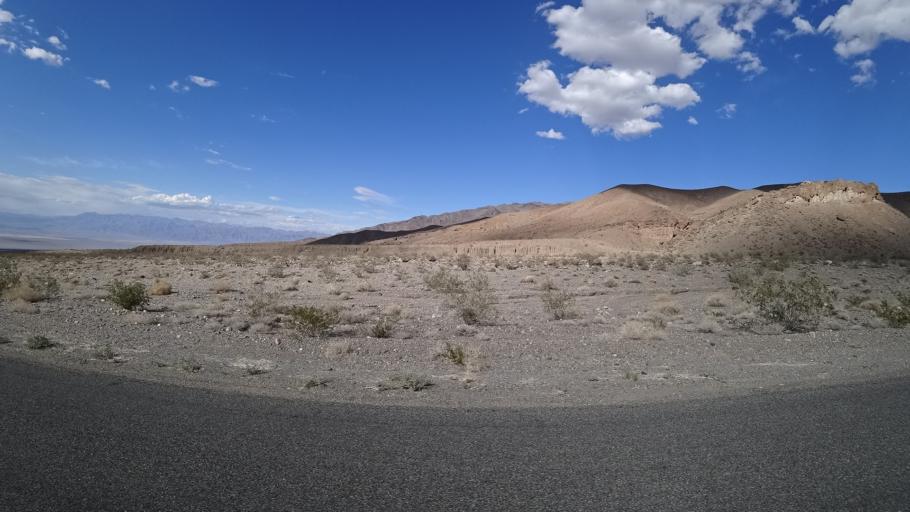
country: US
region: Nevada
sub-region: Nye County
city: Beatty
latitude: 36.4781
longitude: -117.2164
